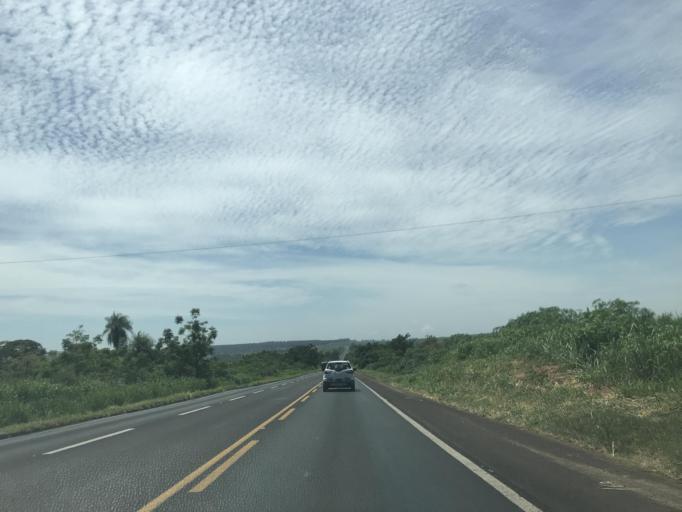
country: BR
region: Parana
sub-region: Paranavai
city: Nova Aurora
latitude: -22.9958
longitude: -52.5831
